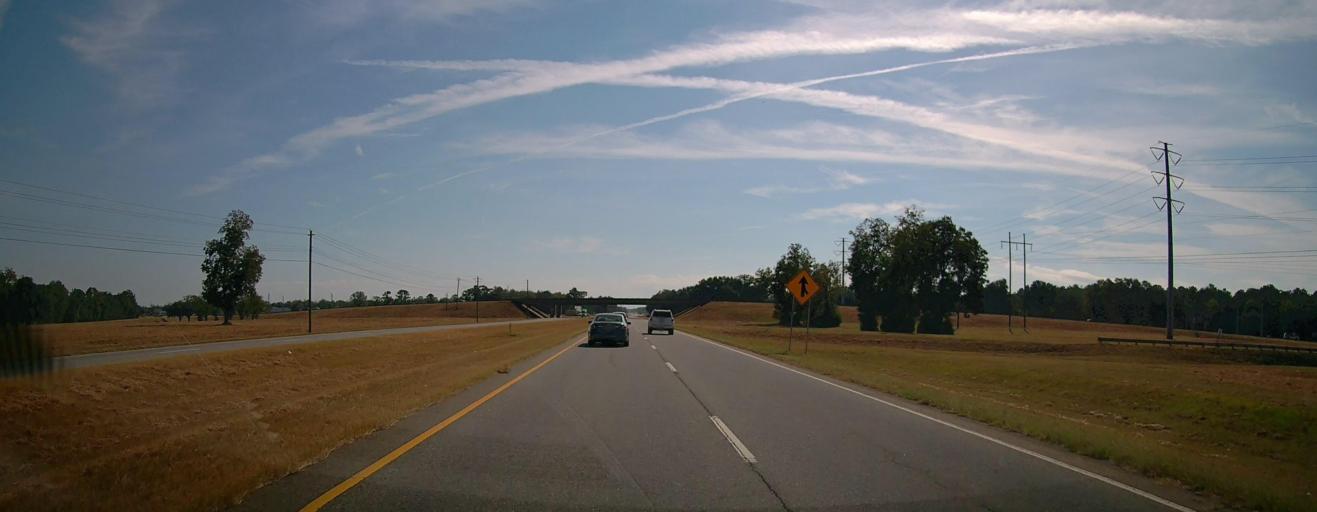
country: US
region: Georgia
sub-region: Dougherty County
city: Albany
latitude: 31.5489
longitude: -84.1151
